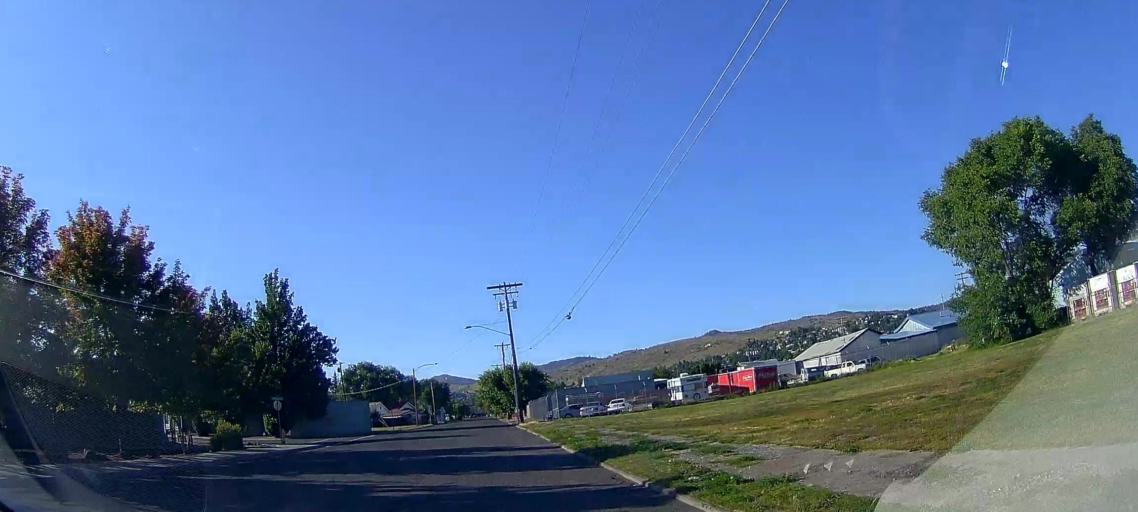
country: US
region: Oregon
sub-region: Klamath County
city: Klamath Falls
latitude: 42.2232
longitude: -121.7767
